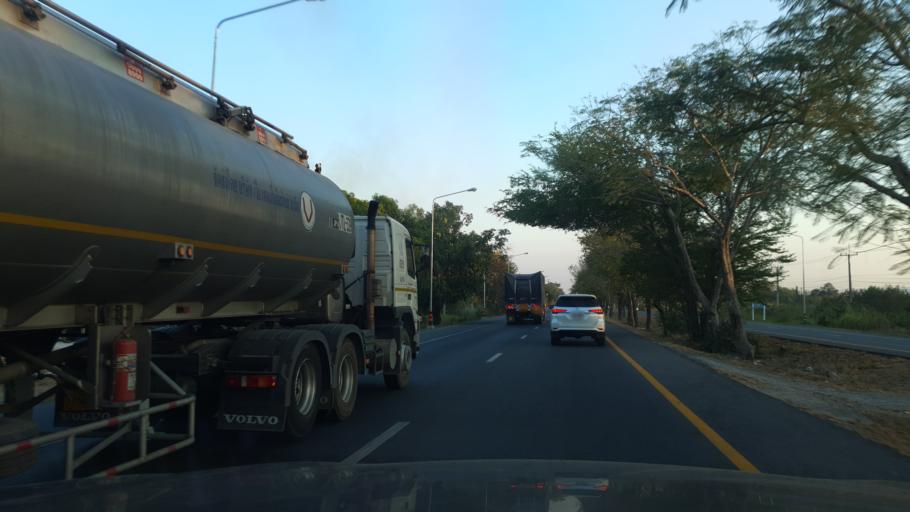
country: TH
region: Nakhon Sawan
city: Banphot Phisai
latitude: 15.8589
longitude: 99.9185
